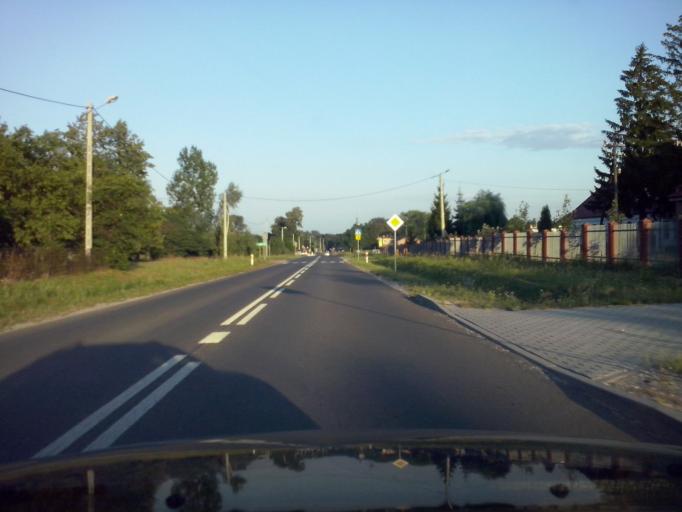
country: PL
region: Swietokrzyskie
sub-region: Powiat buski
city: Gnojno
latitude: 50.6047
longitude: 20.8398
